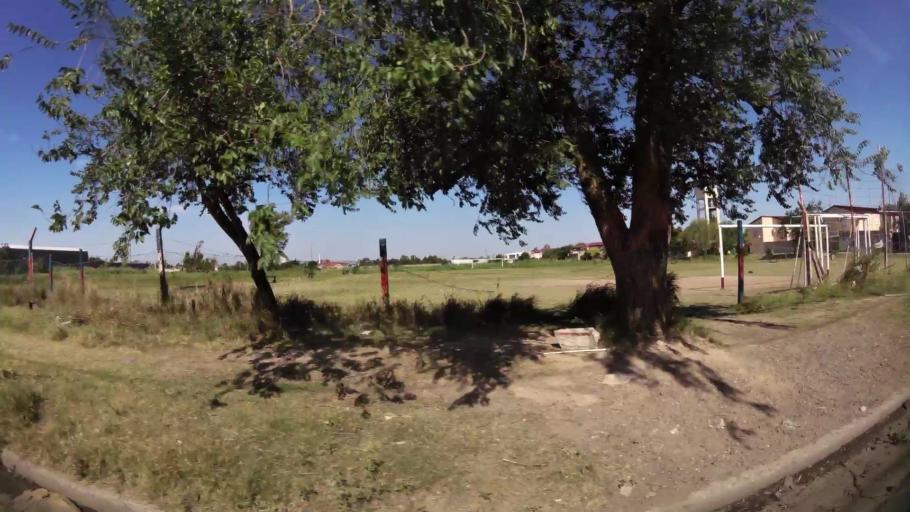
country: AR
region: Cordoba
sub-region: Departamento de Capital
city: Cordoba
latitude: -31.3632
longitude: -64.1838
